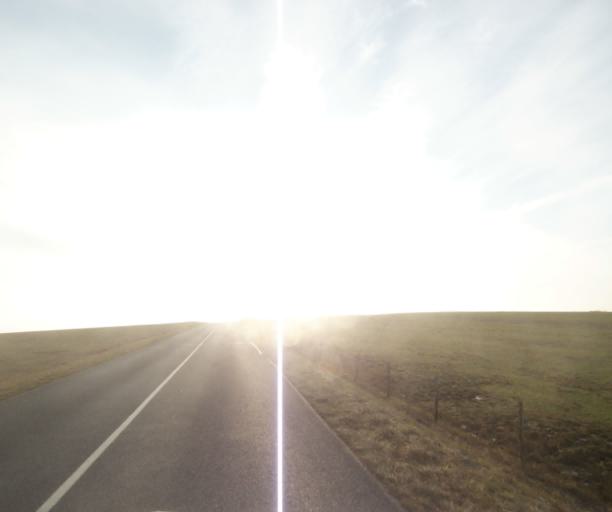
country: FR
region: Champagne-Ardenne
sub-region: Departement de la Marne
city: Sermaize-les-Bains
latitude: 48.7327
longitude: 4.9301
